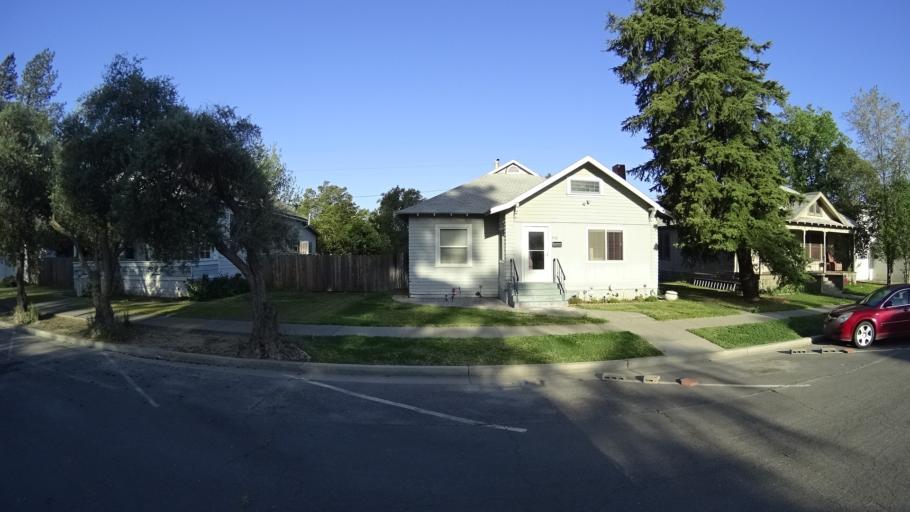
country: US
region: California
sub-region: Glenn County
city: Orland
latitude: 39.7447
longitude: -122.1942
